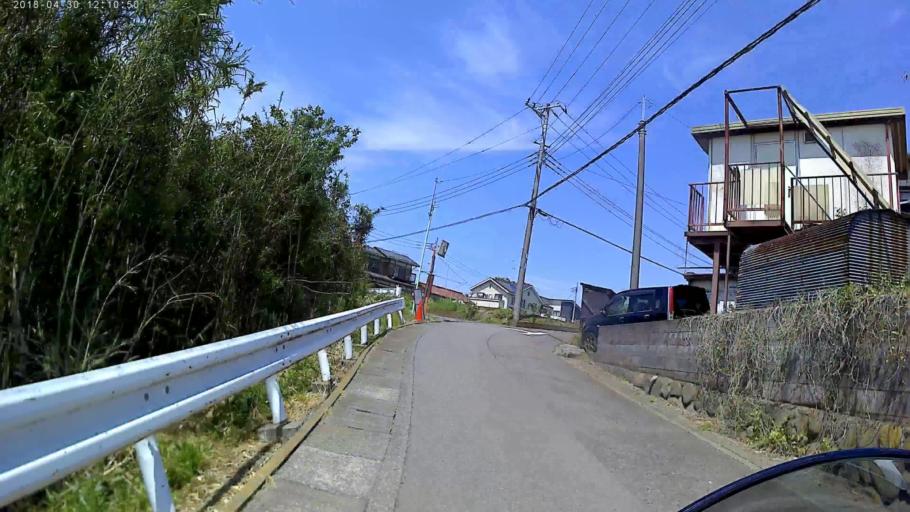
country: JP
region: Kanagawa
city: Zama
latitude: 35.5327
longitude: 139.3104
